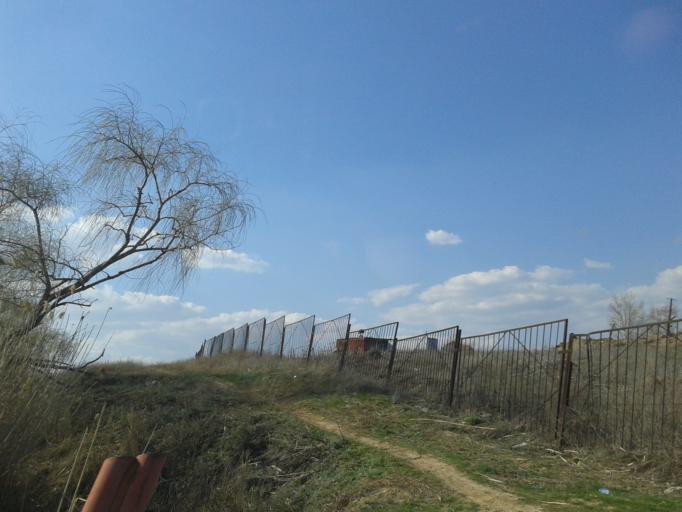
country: RU
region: Volgograd
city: Volgograd
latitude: 48.6286
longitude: 44.3824
